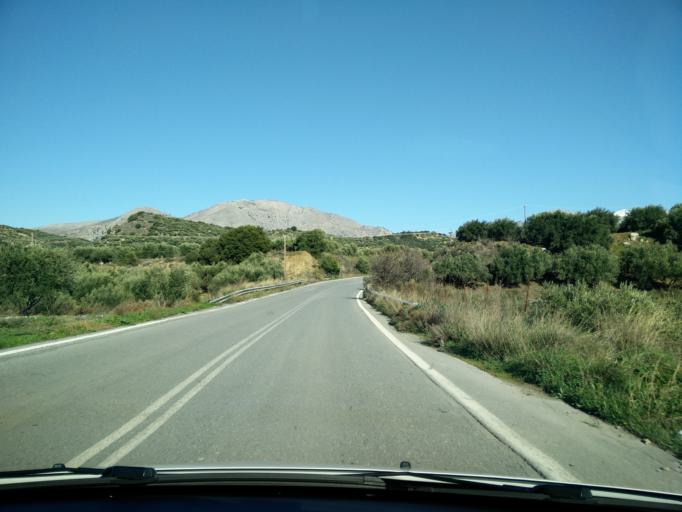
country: GR
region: Crete
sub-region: Nomos Irakleiou
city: Arkalochori
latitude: 35.0776
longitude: 25.3493
